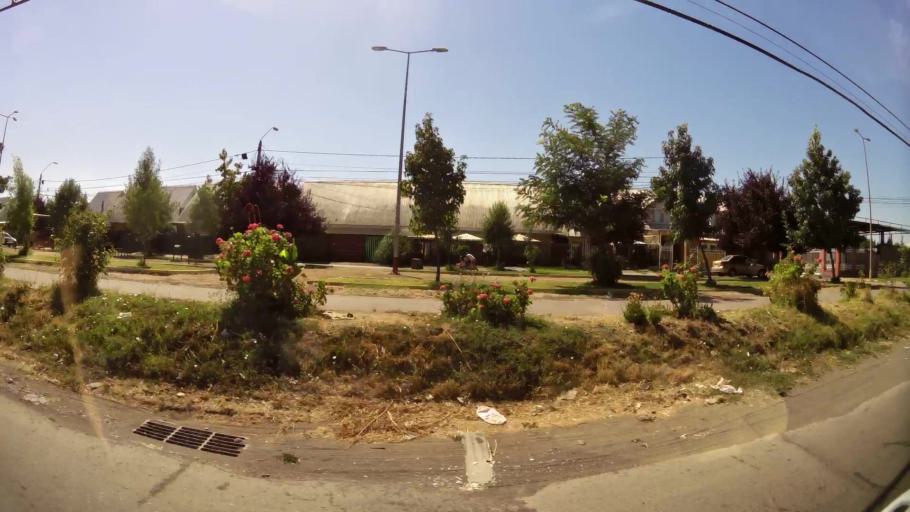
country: CL
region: Maule
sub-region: Provincia de Curico
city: Curico
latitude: -34.9656
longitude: -71.2486
